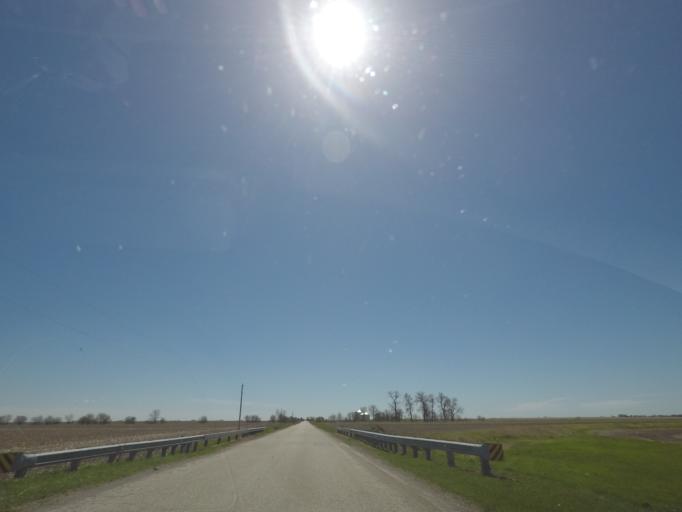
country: US
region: Illinois
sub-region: Logan County
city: Atlanta
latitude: 40.1988
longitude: -89.1942
